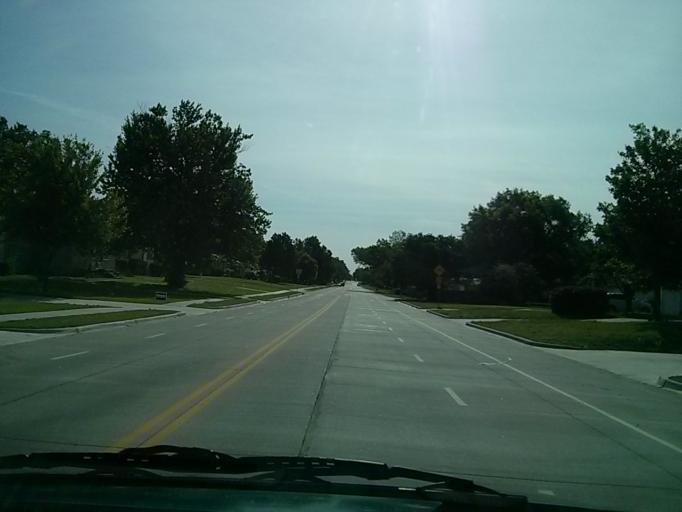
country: US
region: Oklahoma
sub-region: Tulsa County
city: Tulsa
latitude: 36.1551
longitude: -95.9124
